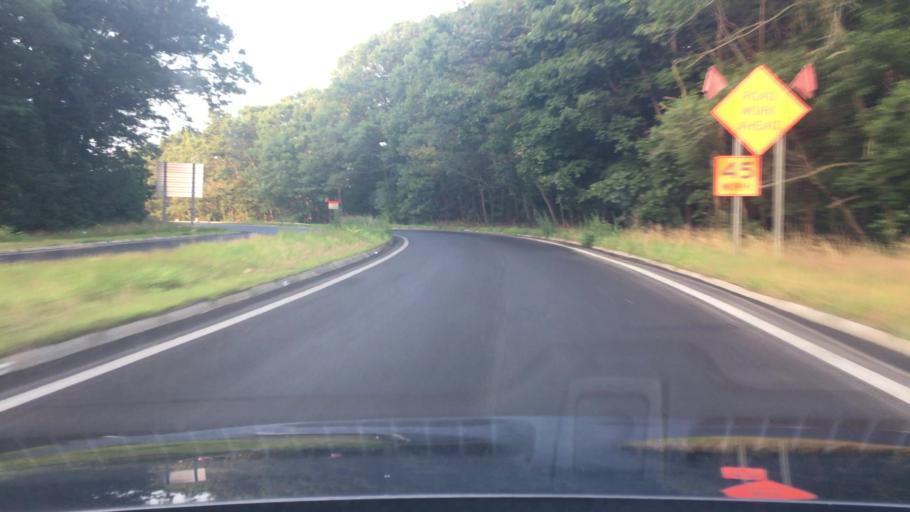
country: US
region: Massachusetts
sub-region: Essex County
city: Amesbury
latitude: 42.8443
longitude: -70.9058
